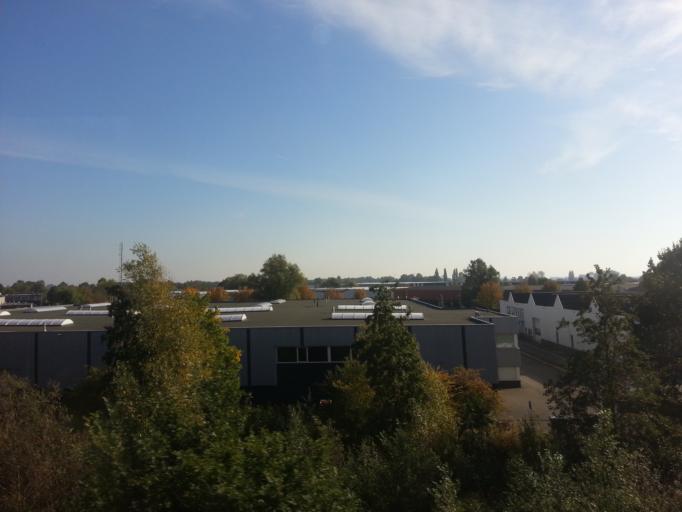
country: NL
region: Gelderland
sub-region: Gemeente Zaltbommel
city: Zaltbommel
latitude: 51.8100
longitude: 5.2630
